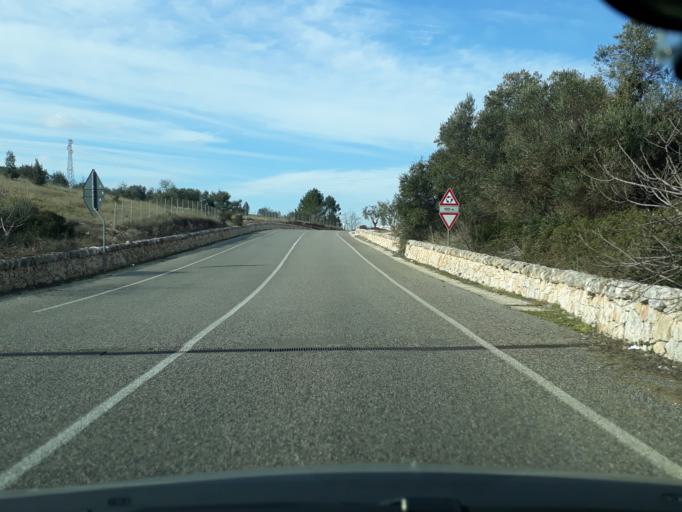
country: IT
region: Apulia
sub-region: Provincia di Bari
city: Locorotondo
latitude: 40.7531
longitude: 17.3452
